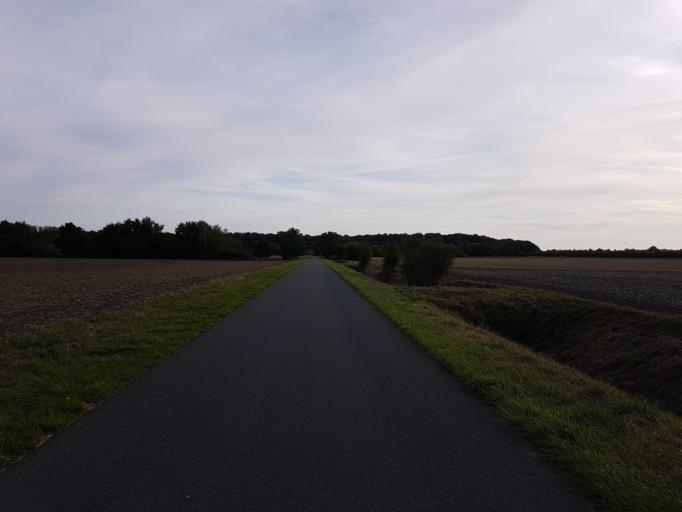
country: DE
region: Lower Saxony
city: Laatzen
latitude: 52.3521
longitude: 9.8696
